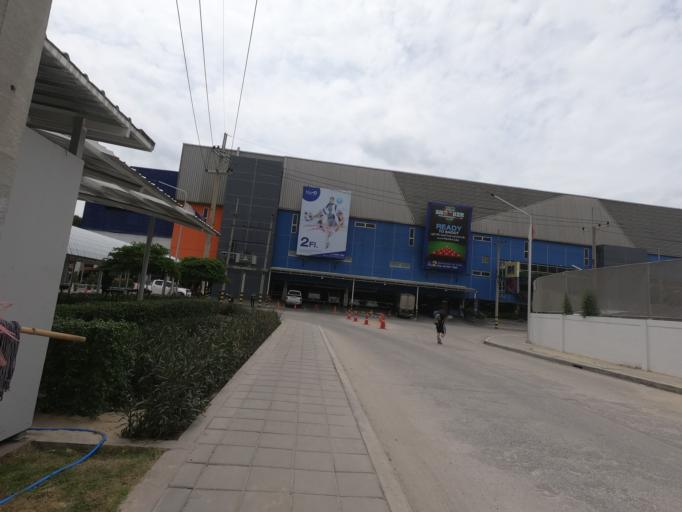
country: TH
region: Bangkok
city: Sai Mai
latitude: 13.9376
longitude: 100.6526
